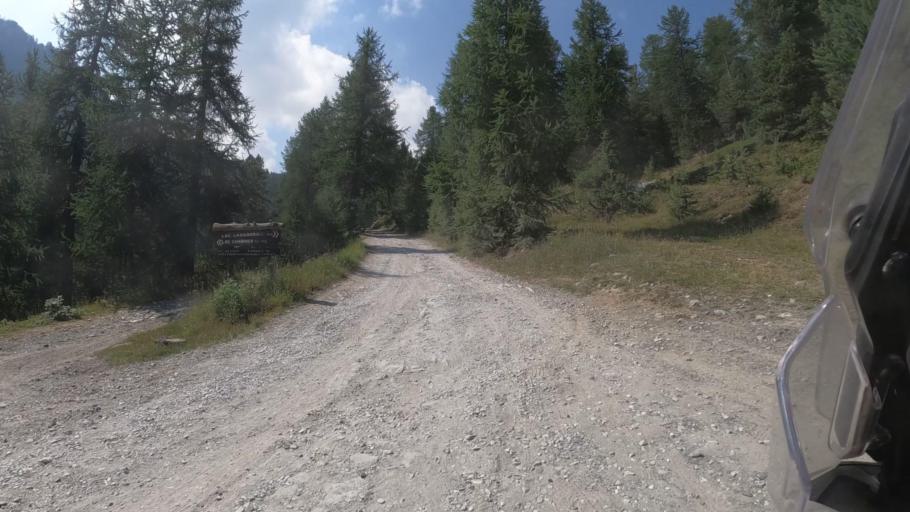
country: IT
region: Piedmont
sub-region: Provincia di Torino
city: Cesana Torinese
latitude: 44.9108
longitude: 6.8003
